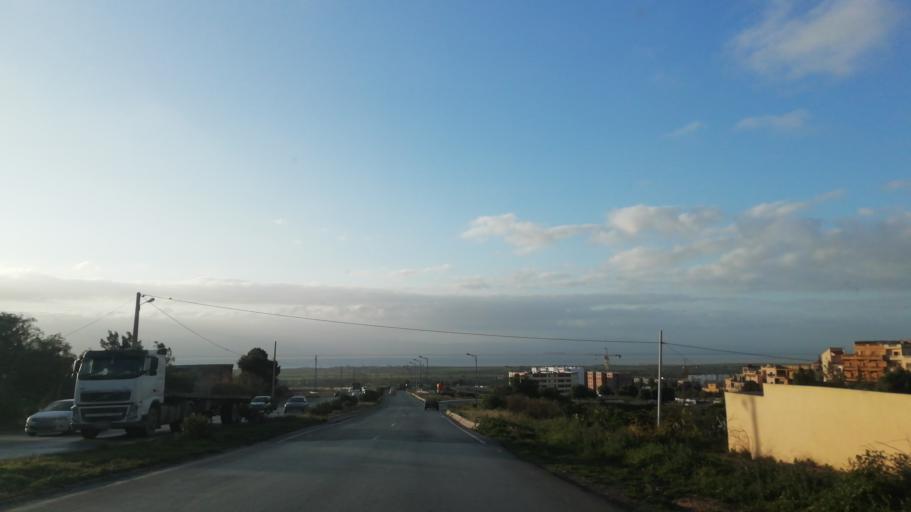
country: DZ
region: Oran
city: Es Senia
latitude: 35.6245
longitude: -0.7188
